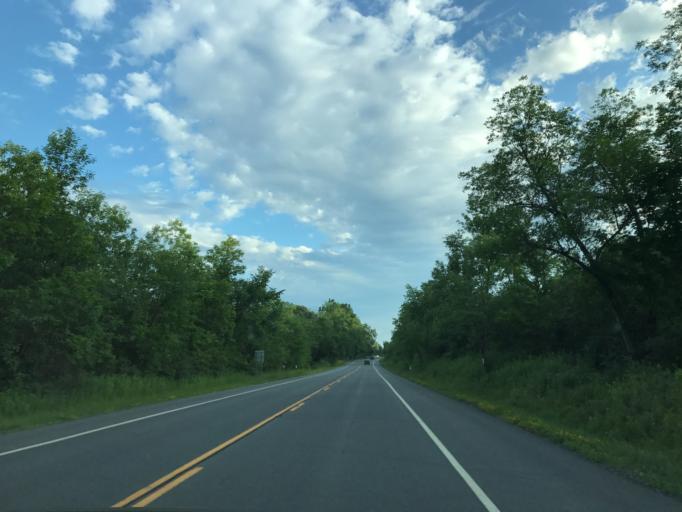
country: US
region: New York
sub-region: Saratoga County
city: Stillwater
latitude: 42.9977
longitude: -73.6110
